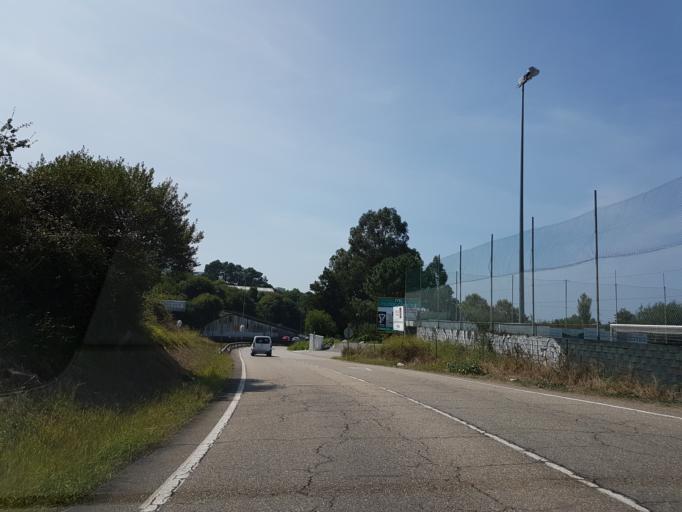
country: ES
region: Galicia
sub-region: Provincia de Pontevedra
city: Vigo
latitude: 42.2165
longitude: -8.6776
